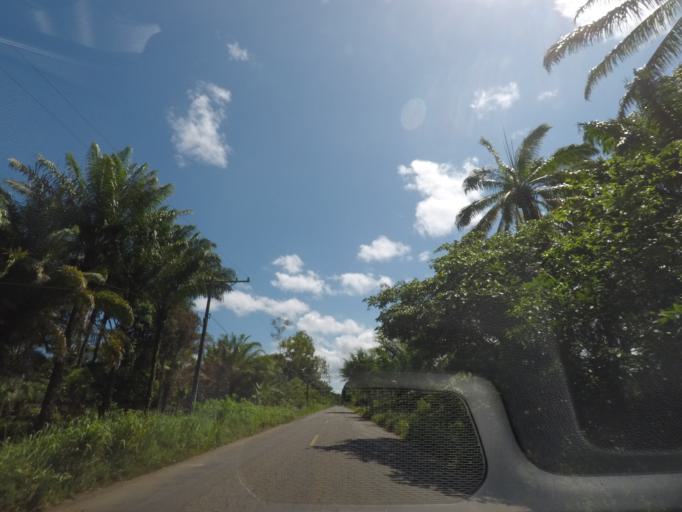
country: BR
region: Bahia
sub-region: Taperoa
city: Taperoa
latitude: -13.4878
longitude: -39.0920
